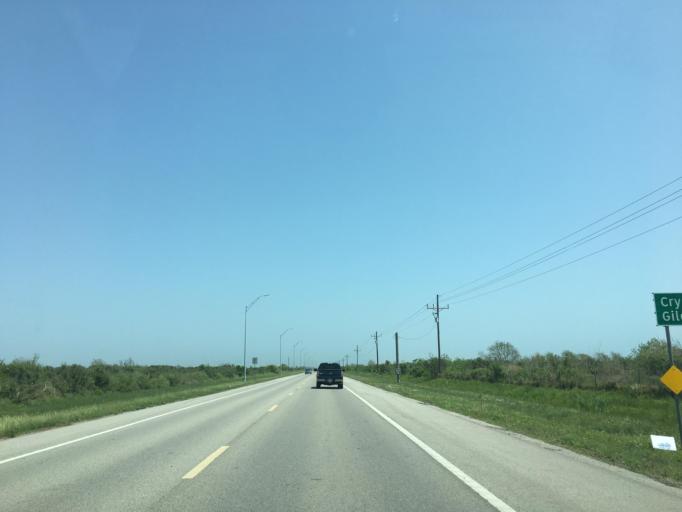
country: US
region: Texas
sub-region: Galveston County
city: Galveston
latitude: 29.3815
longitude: -94.7438
